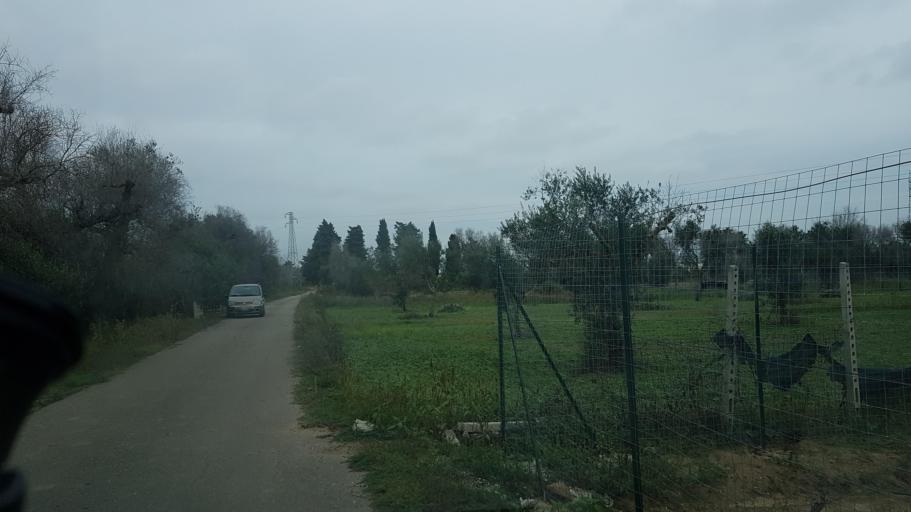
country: IT
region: Apulia
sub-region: Provincia di Brindisi
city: San Donaci
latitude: 40.4516
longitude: 17.9360
